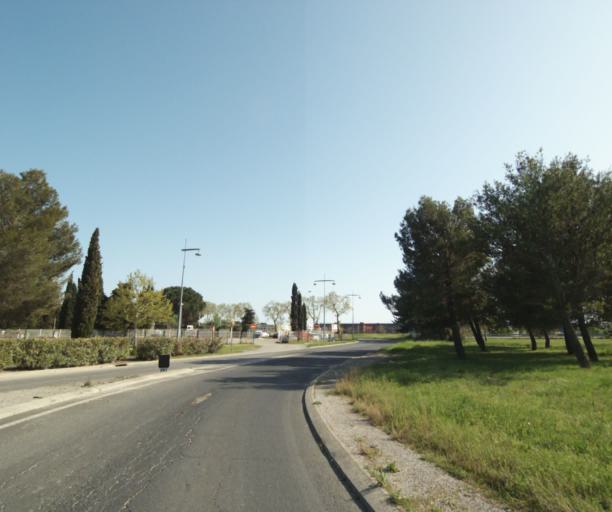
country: FR
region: Languedoc-Roussillon
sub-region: Departement de l'Herault
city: Juvignac
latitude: 43.6187
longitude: 3.7951
